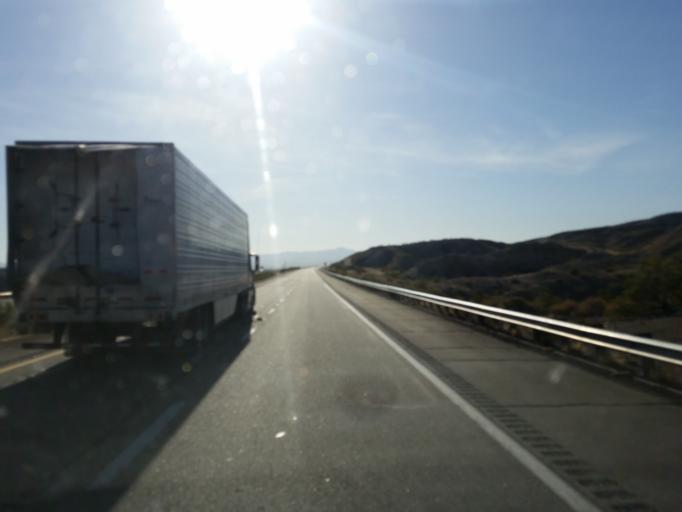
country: US
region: Arizona
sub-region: Mohave County
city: Desert Hills
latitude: 34.7256
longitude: -114.4049
